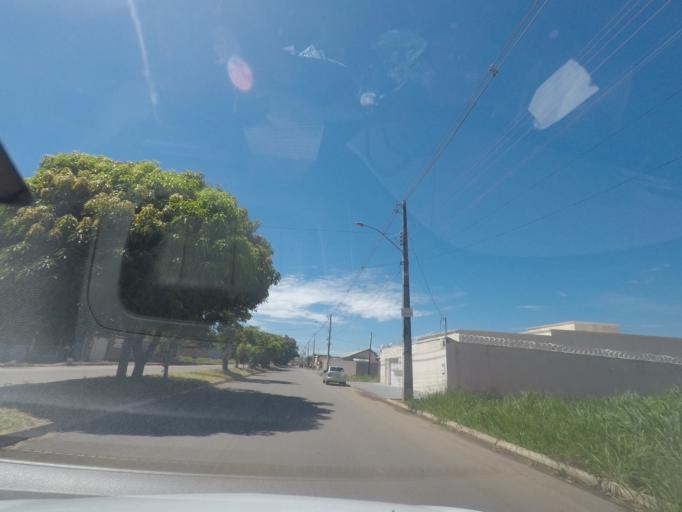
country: BR
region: Goias
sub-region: Aparecida De Goiania
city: Aparecida de Goiania
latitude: -16.7805
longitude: -49.3370
